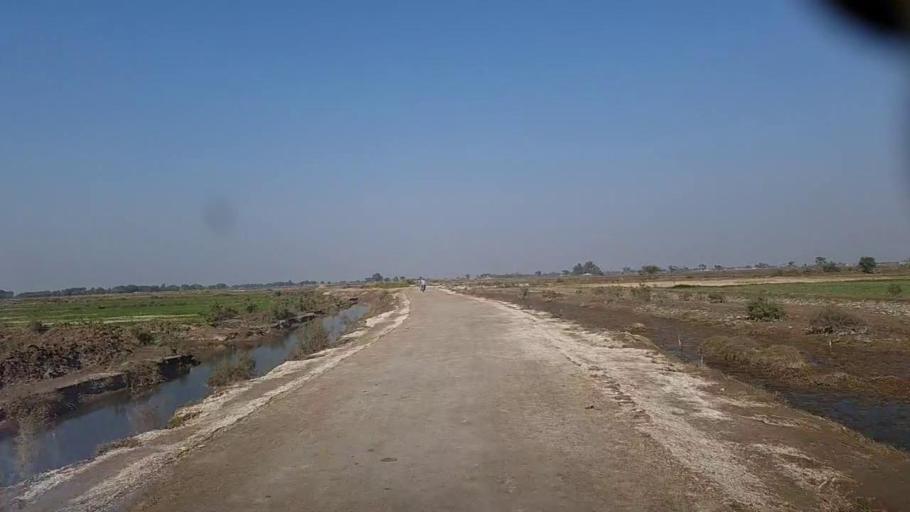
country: PK
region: Sindh
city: Jacobabad
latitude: 28.3080
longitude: 68.5614
